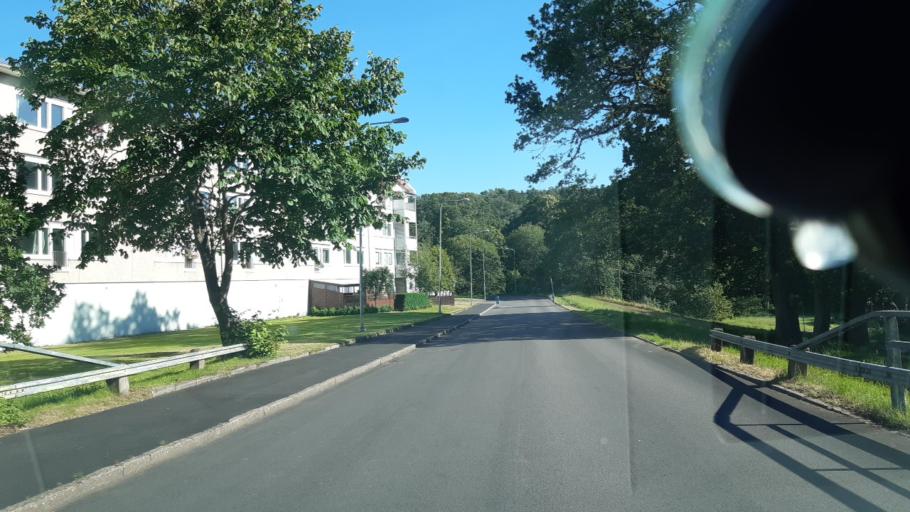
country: SE
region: Vaestra Goetaland
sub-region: Goteborg
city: Eriksbo
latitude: 57.7702
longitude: 12.0341
